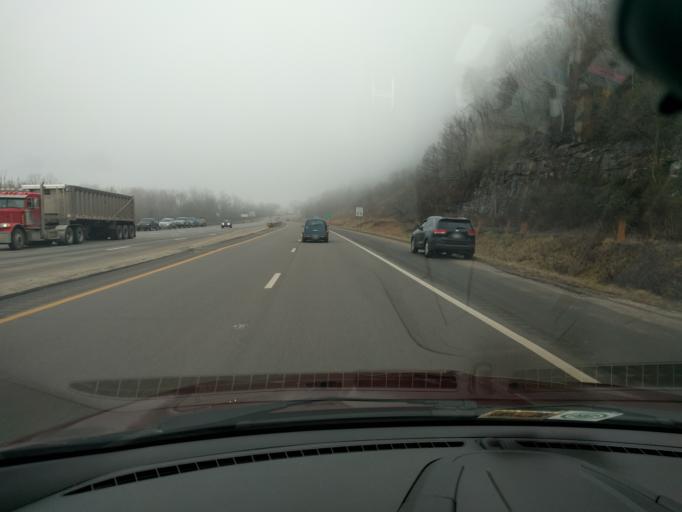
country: US
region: West Virginia
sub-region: Kanawha County
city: Chesapeake
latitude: 38.2114
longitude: -81.5106
